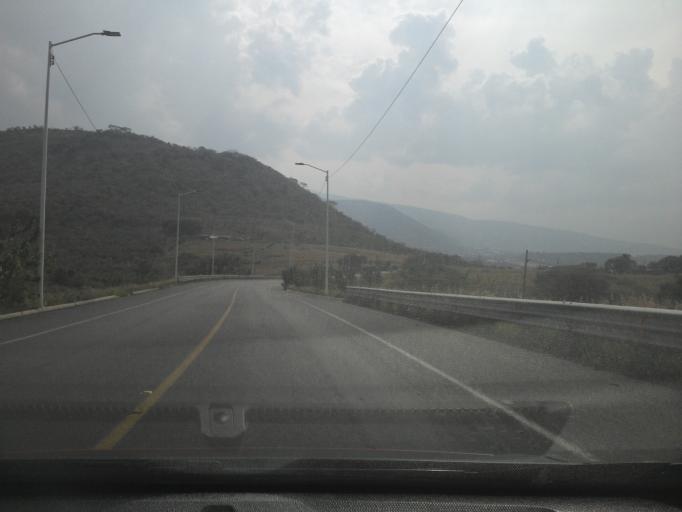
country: MX
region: Jalisco
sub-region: Tlajomulco de Zuniga
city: El Cortijo
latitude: 20.4827
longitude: -103.4310
